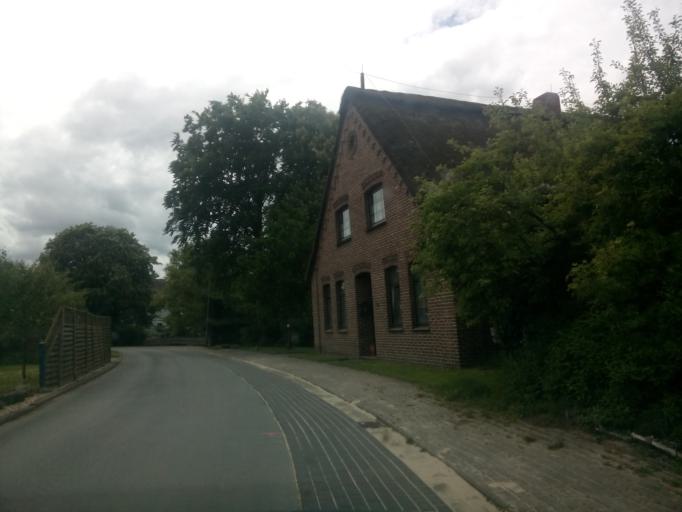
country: DE
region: Lower Saxony
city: Lemwerder
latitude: 53.1528
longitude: 8.6156
